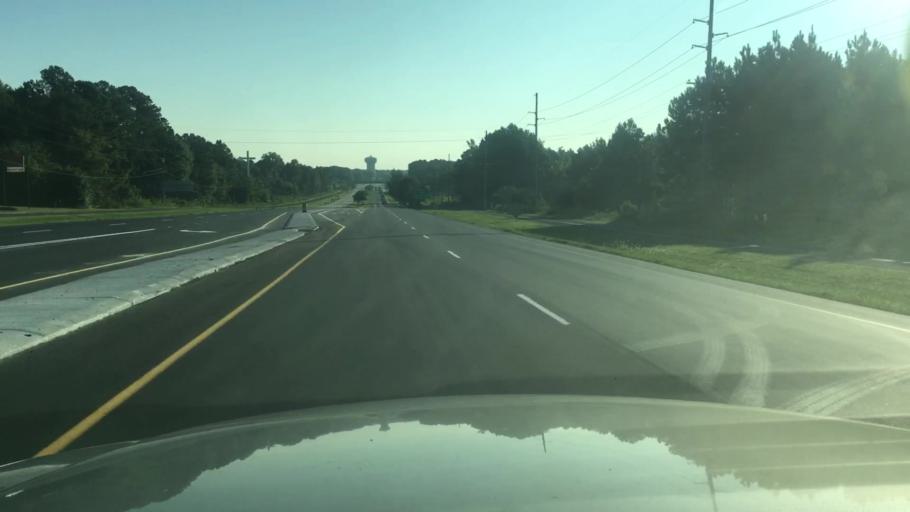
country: US
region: North Carolina
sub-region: Cumberland County
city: Fayetteville
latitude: 35.0268
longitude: -78.8865
